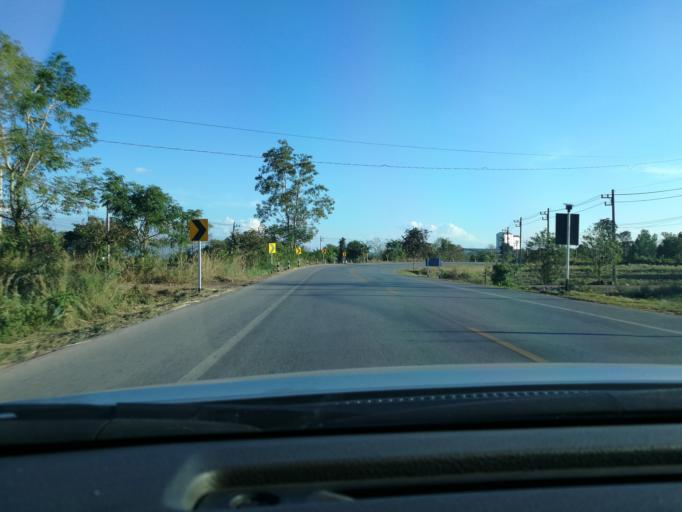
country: TH
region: Phitsanulok
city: Nakhon Thai
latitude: 17.0553
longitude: 100.8108
